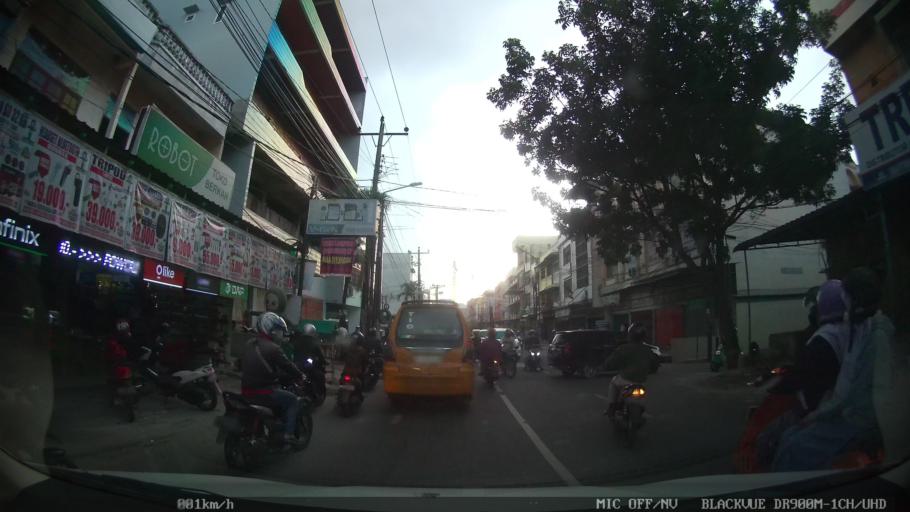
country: ID
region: North Sumatra
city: Medan
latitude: 3.5823
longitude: 98.7010
